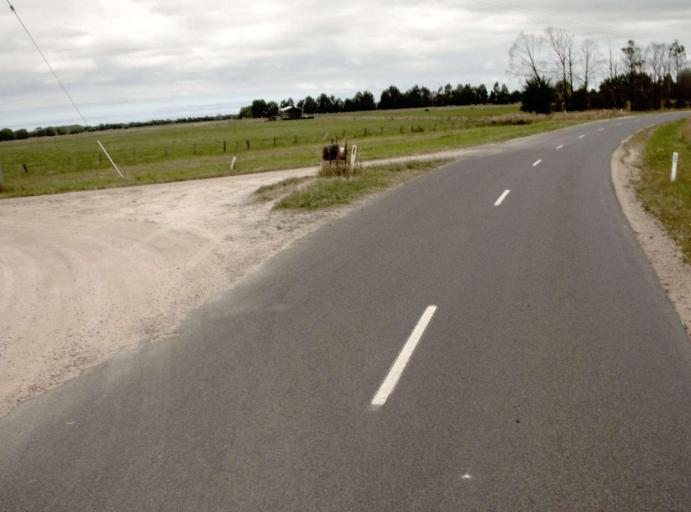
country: AU
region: Victoria
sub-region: Latrobe
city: Traralgon
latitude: -38.4967
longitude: 146.6785
